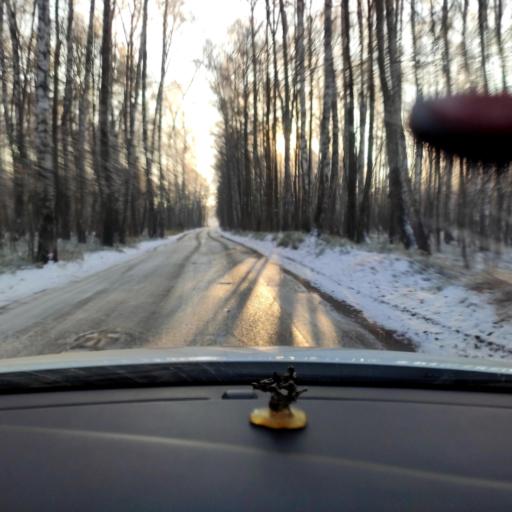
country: RU
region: Tatarstan
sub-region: Gorod Kazan'
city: Kazan
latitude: 55.6754
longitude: 49.1024
